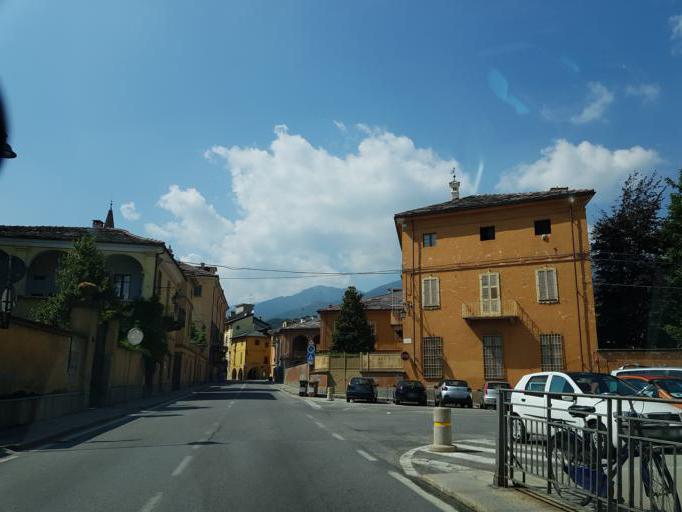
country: IT
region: Piedmont
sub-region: Provincia di Cuneo
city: Dronero
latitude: 44.4664
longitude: 7.3649
